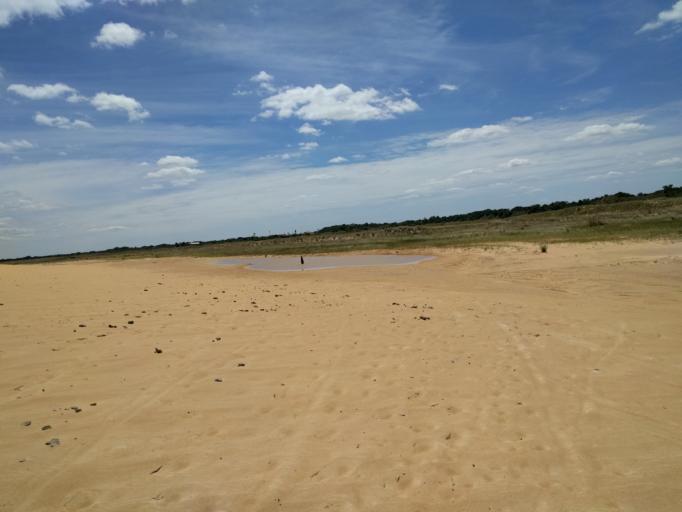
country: BO
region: Santa Cruz
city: Santa Cruz de la Sierra
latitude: -17.9429
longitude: -63.1535
